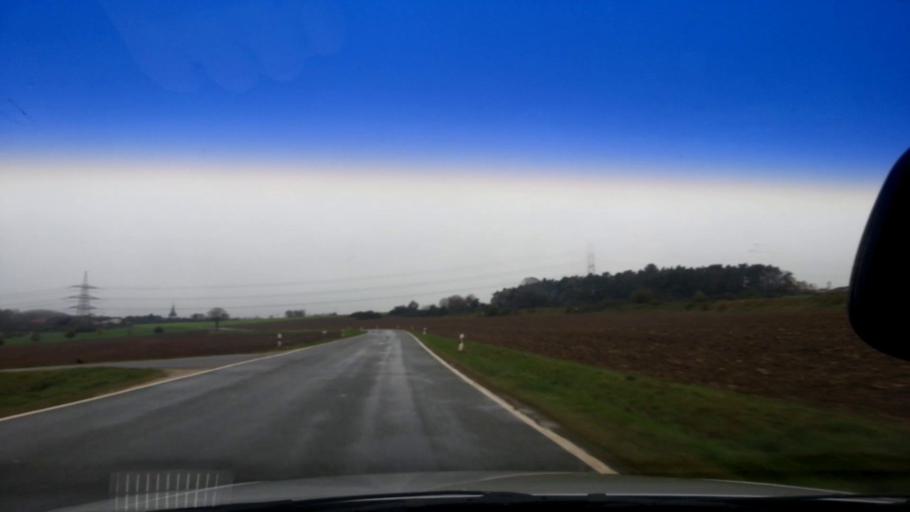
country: DE
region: Bavaria
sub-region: Upper Franconia
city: Wattendorf
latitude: 50.0353
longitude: 11.1376
